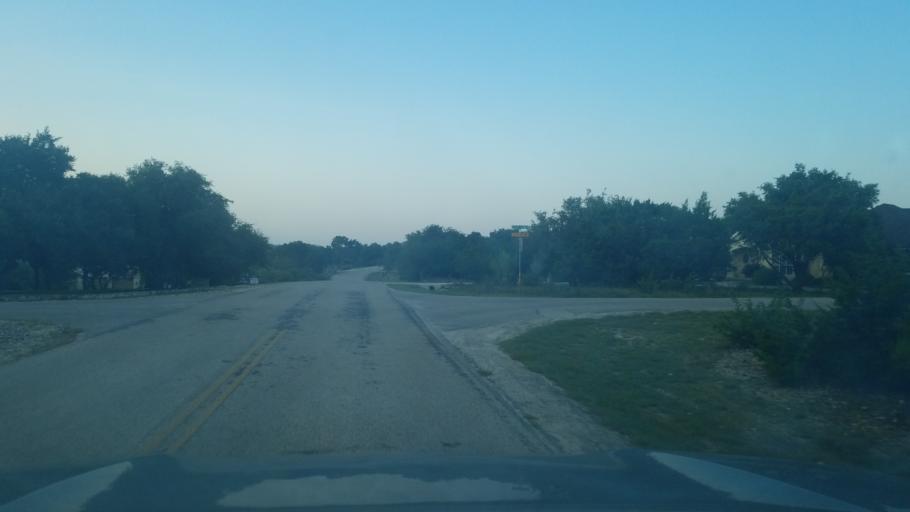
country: US
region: Texas
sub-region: Comal County
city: Bulverde
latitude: 29.8287
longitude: -98.4031
